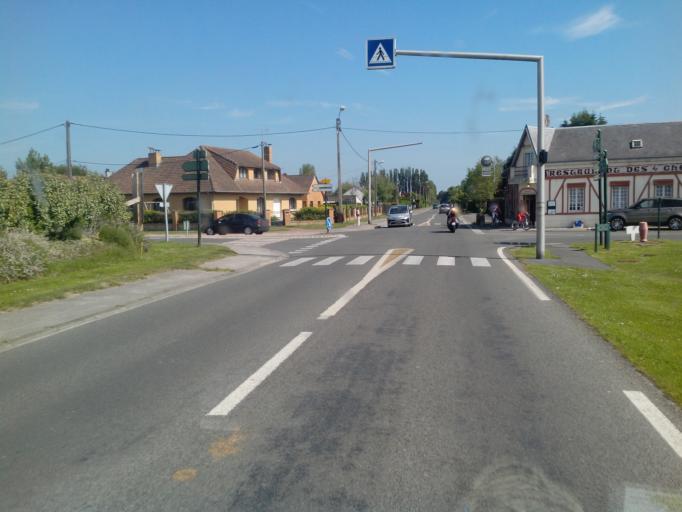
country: FR
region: Nord-Pas-de-Calais
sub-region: Departement du Pas-de-Calais
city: Groffliers
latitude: 50.3882
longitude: 1.6095
